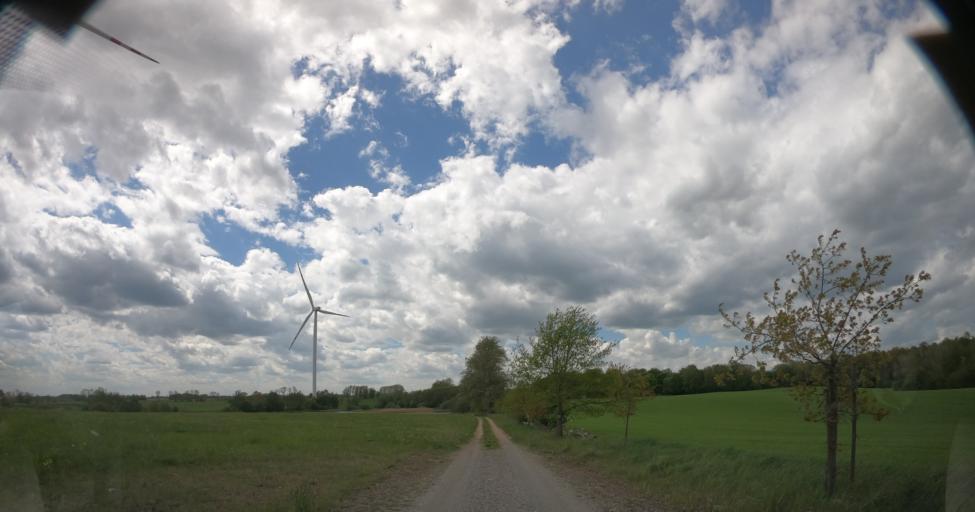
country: PL
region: West Pomeranian Voivodeship
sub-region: Powiat drawski
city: Drawsko Pomorskie
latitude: 53.5631
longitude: 15.7808
